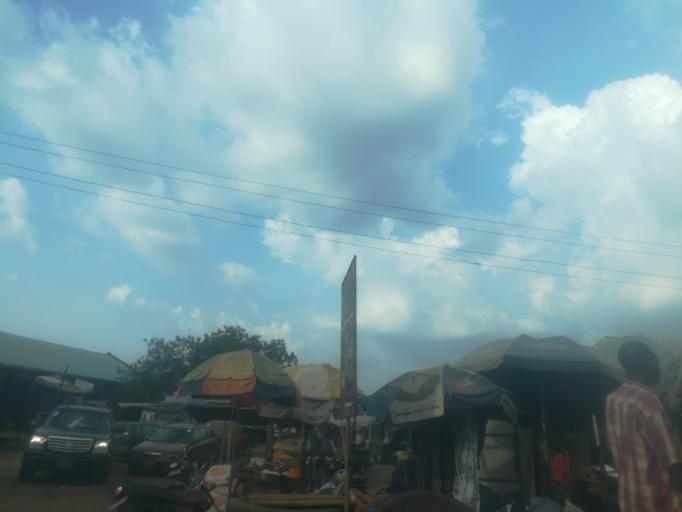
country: NG
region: Ogun
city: Abeokuta
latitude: 7.1461
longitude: 3.3174
